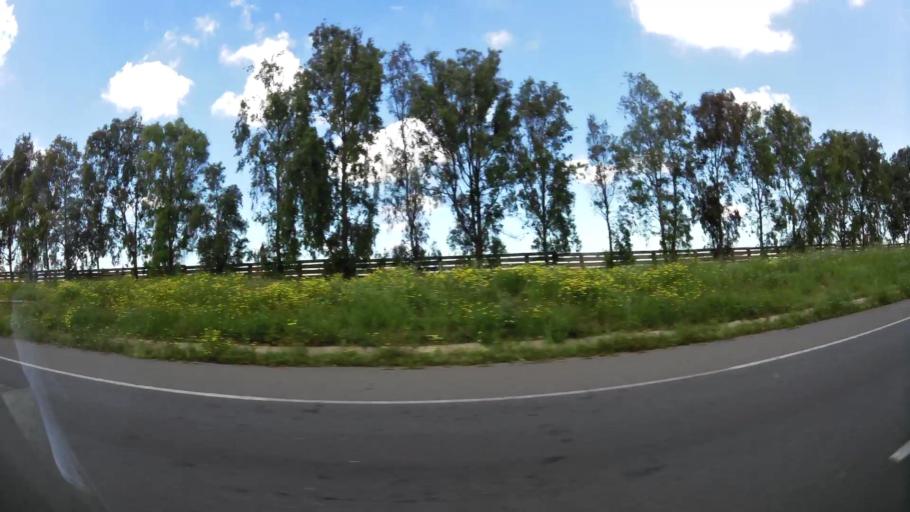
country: MA
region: Grand Casablanca
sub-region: Casablanca
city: Casablanca
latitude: 33.5195
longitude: -7.5811
